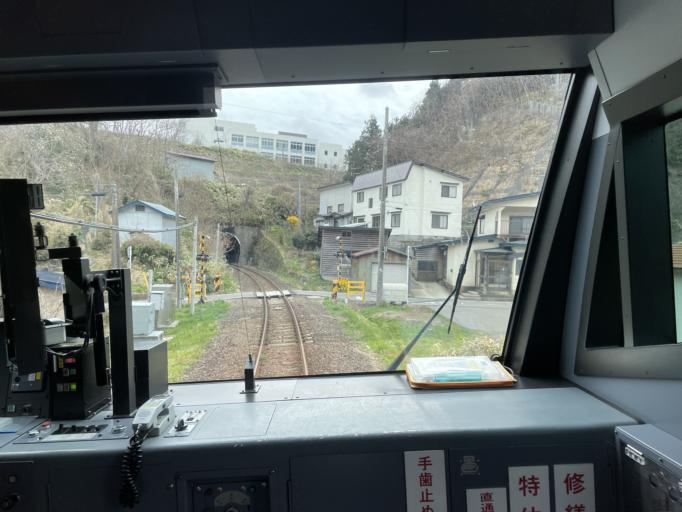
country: JP
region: Akita
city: Noshiromachi
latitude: 40.6397
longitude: 139.9255
